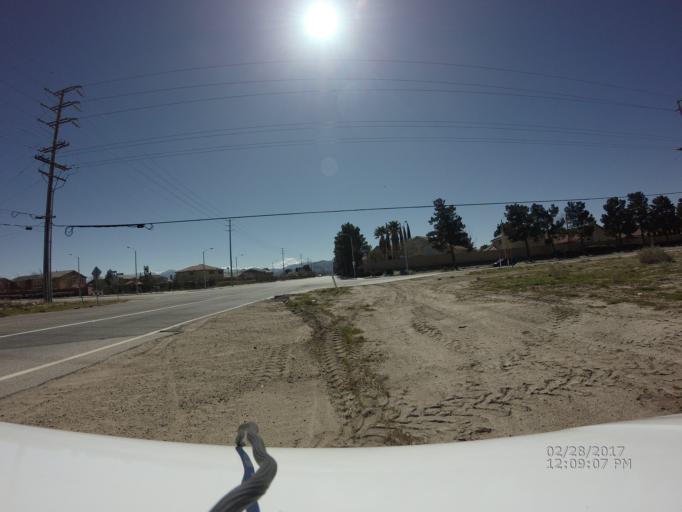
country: US
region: California
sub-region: Los Angeles County
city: Palmdale
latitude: 34.5878
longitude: -118.0586
